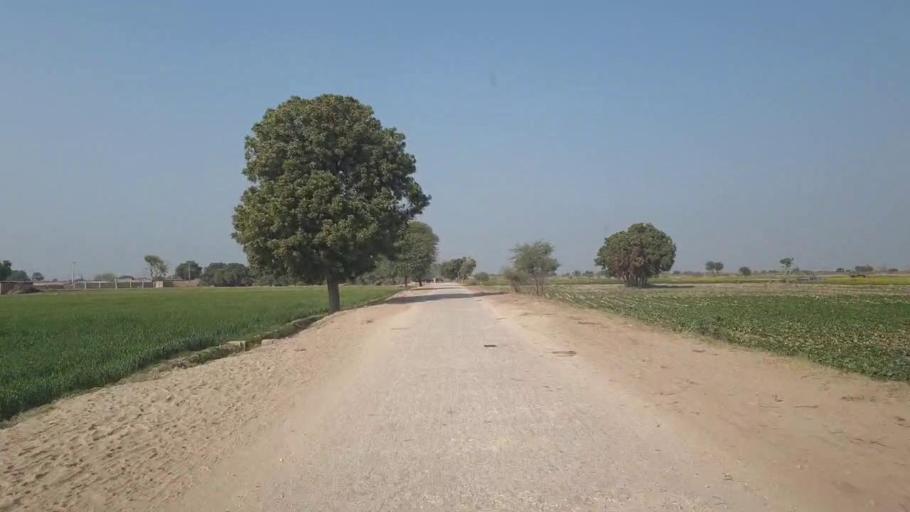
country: PK
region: Sindh
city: Tando Allahyar
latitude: 25.4406
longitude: 68.7874
